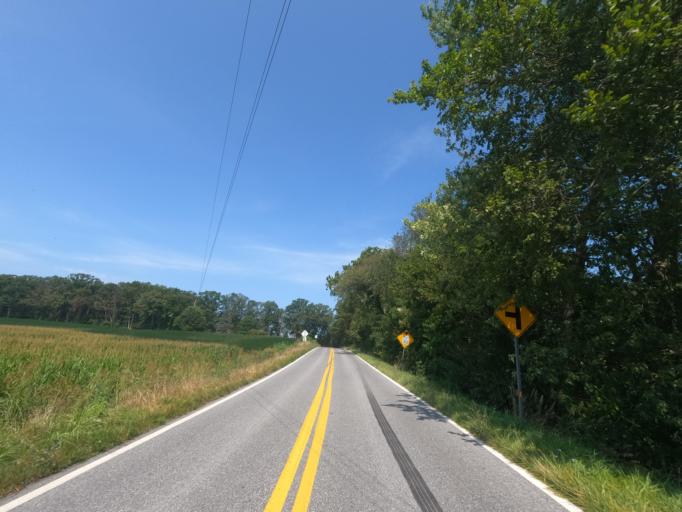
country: US
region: Pennsylvania
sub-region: Adams County
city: Mount Pleasant
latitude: 39.6528
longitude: -77.0796
